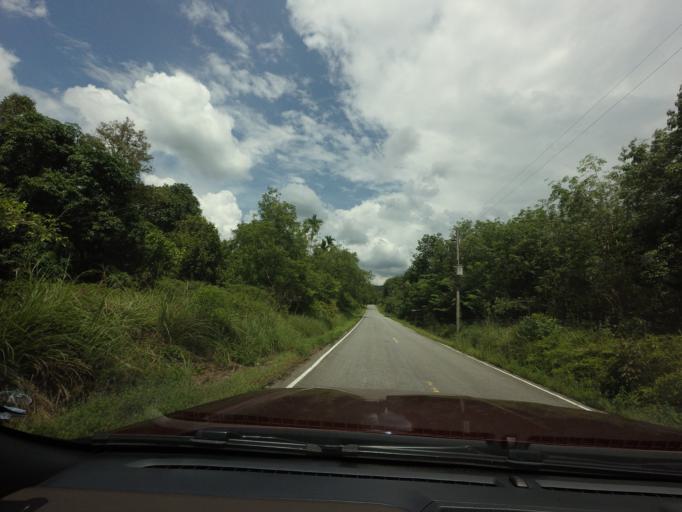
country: TH
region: Narathiwat
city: Chanae
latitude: 6.0500
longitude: 101.6884
